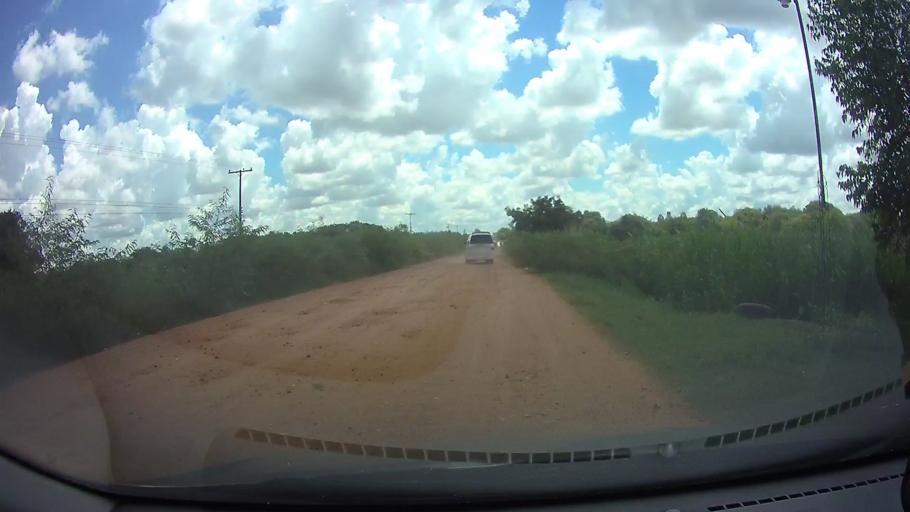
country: PY
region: Presidente Hayes
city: Nanawa
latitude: -25.2500
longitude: -57.6487
